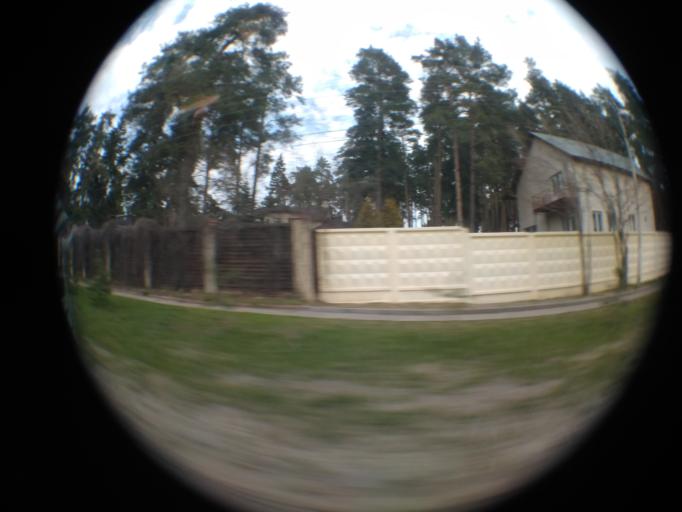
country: RU
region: Moskovskaya
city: Zhukovskiy
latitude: 55.5922
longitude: 38.1468
